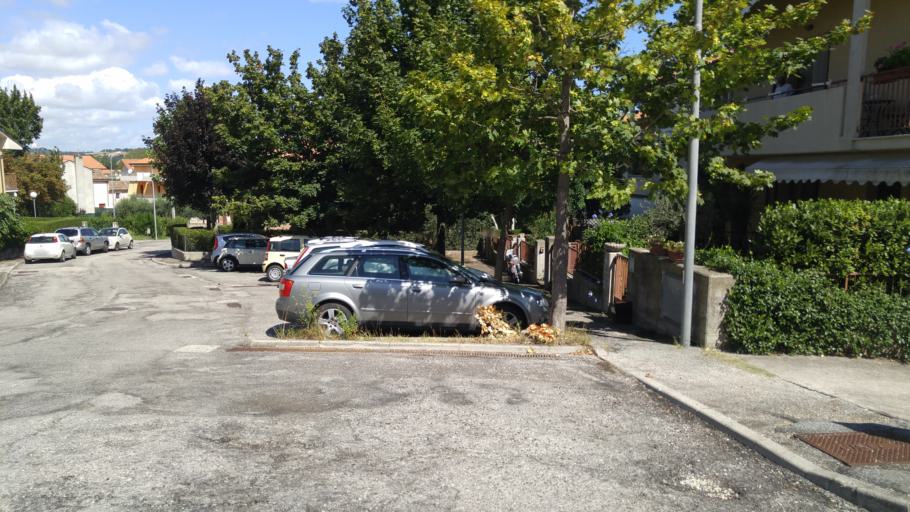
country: IT
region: The Marches
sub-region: Provincia di Pesaro e Urbino
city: Centinarola
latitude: 43.8304
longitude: 12.9858
